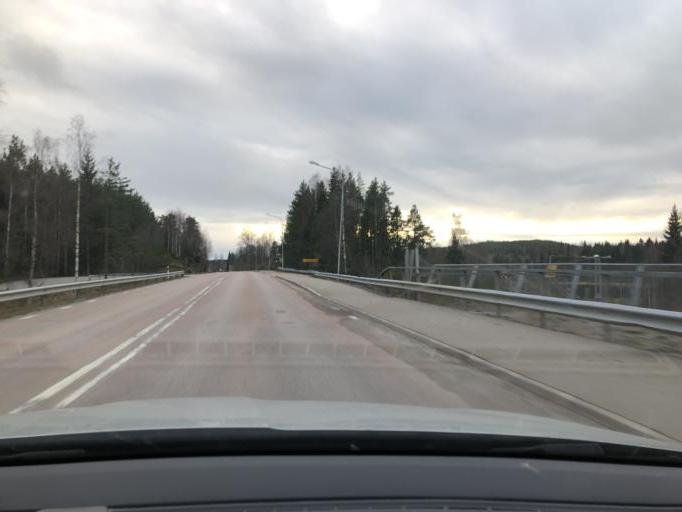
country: SE
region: Gaevleborg
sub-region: Hudiksvalls Kommun
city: Iggesund
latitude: 61.6266
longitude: 17.0560
